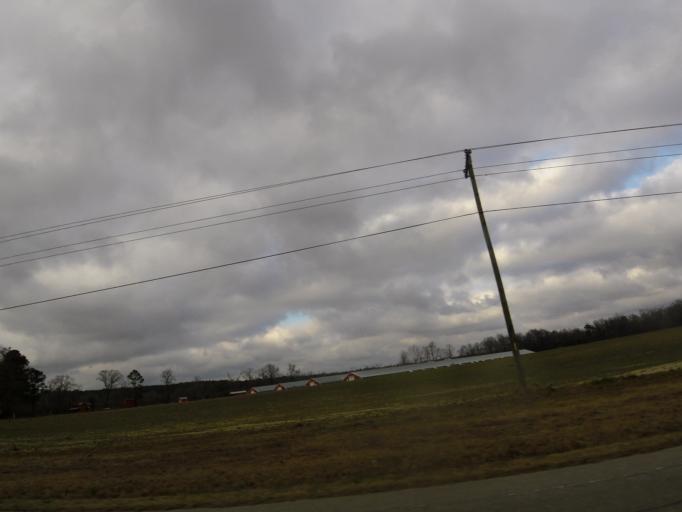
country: US
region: North Carolina
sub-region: Edgecombe County
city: Pinetops
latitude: 35.8530
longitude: -77.6750
